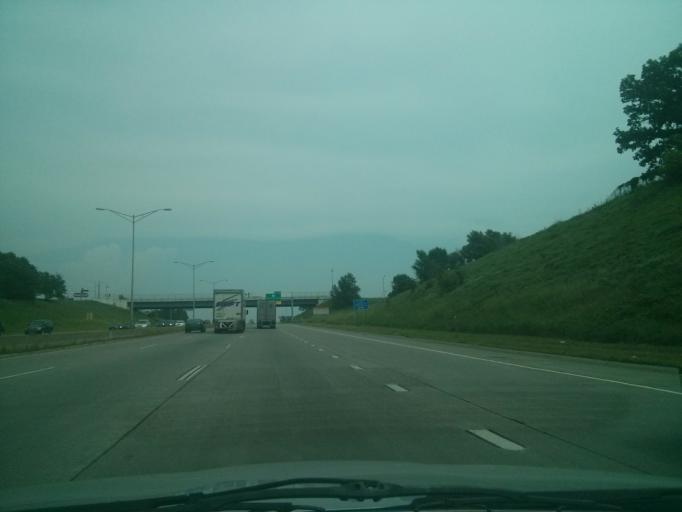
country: US
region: Wisconsin
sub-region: Saint Croix County
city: Hudson
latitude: 44.9627
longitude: -92.7480
